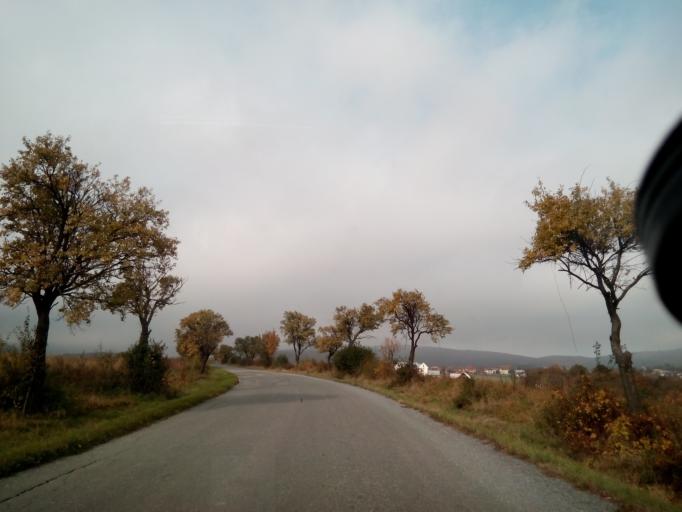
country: SK
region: Kosicky
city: Kosice
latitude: 48.7350
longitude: 21.1285
